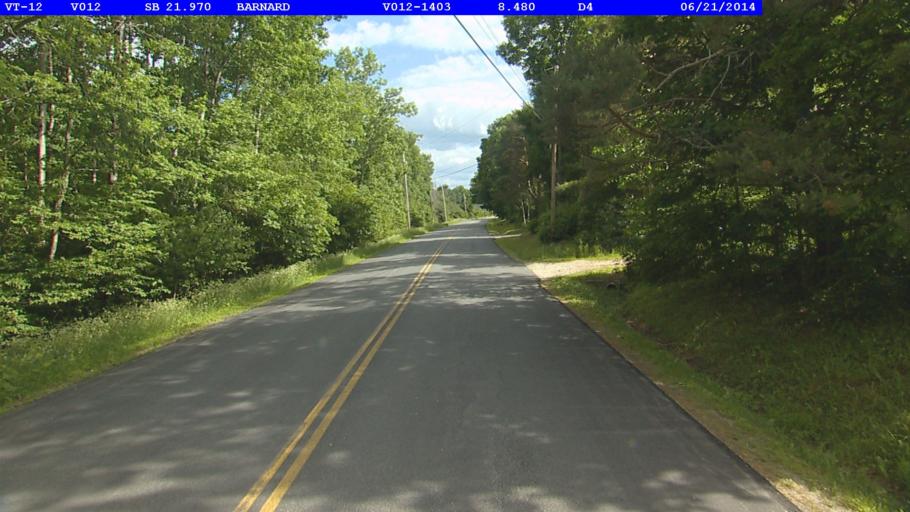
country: US
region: Vermont
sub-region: Orange County
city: Randolph
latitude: 43.7777
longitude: -72.6365
